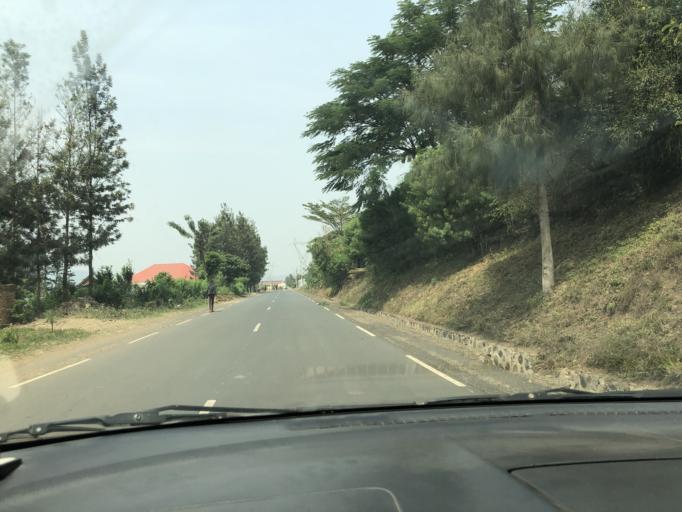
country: BI
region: Cibitoke
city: Cibitoke
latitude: -2.6965
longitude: 29.0042
